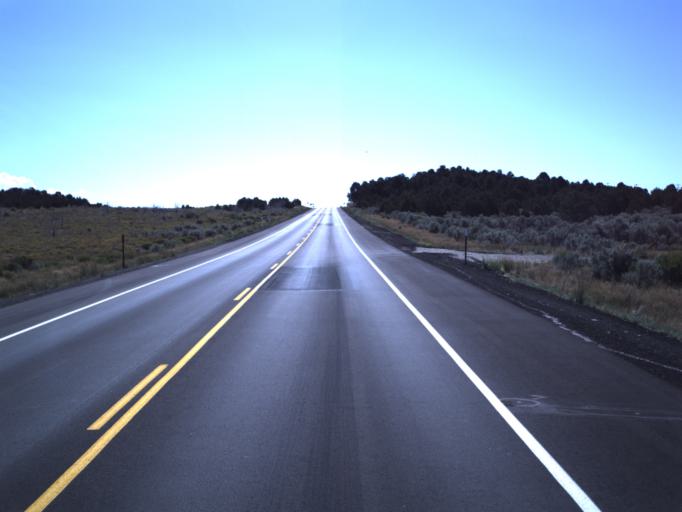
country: US
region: Utah
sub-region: Utah County
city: Genola
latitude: 39.9612
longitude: -112.2474
